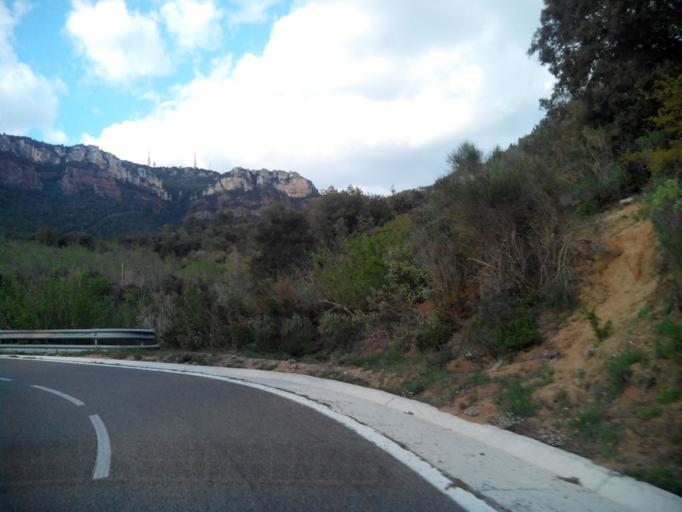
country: ES
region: Catalonia
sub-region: Provincia de Tarragona
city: Vilaplana
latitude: 41.2333
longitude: 1.0431
